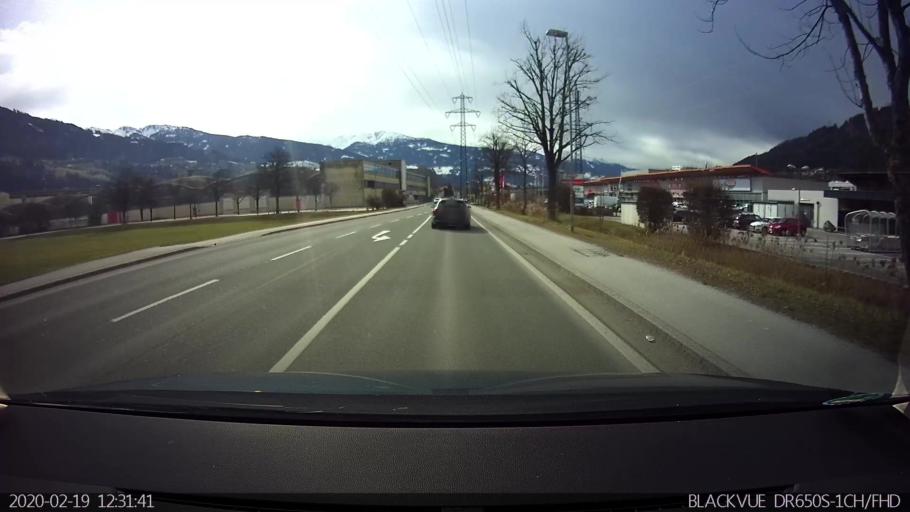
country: AT
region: Tyrol
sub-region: Politischer Bezirk Schwaz
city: Schwaz
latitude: 47.3505
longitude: 11.6984
